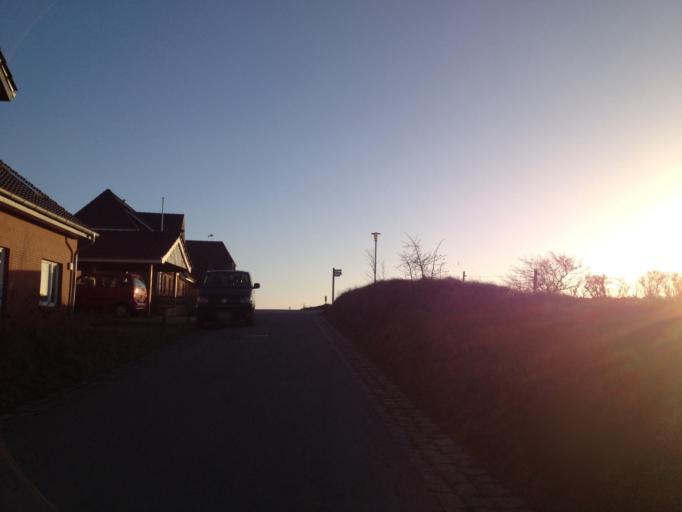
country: DE
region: Schleswig-Holstein
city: Nebel
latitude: 54.6482
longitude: 8.3581
